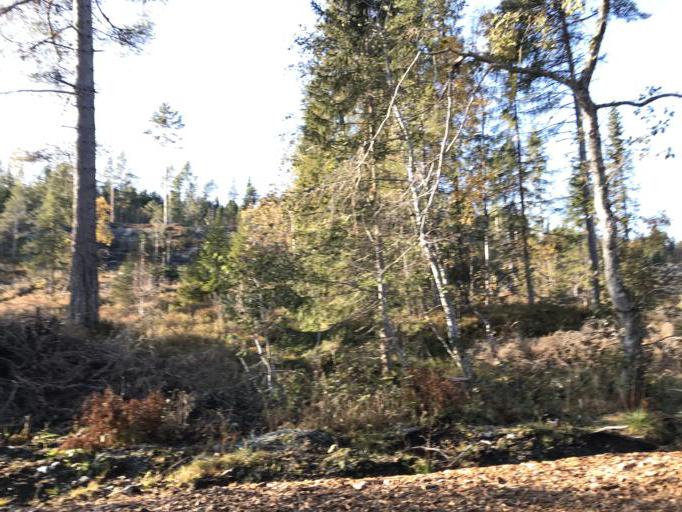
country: NO
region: Sor-Trondelag
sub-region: Trondheim
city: Trondheim
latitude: 63.4136
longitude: 10.3294
